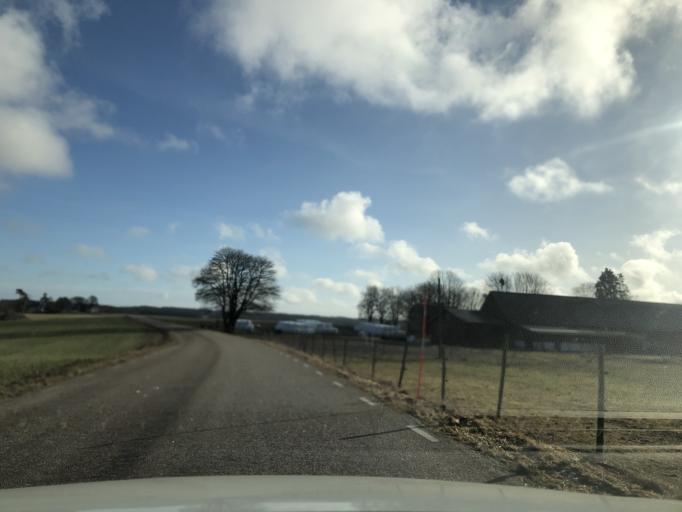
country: SE
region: Vaestra Goetaland
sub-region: Ulricehamns Kommun
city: Ulricehamn
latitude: 57.8003
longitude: 13.5827
